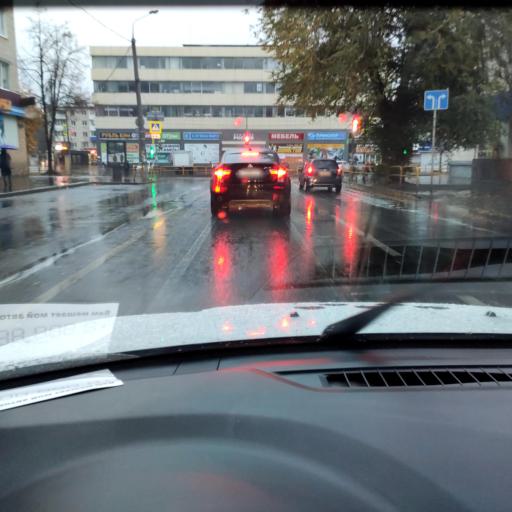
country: RU
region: Samara
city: Tol'yatti
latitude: 53.5064
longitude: 49.4164
